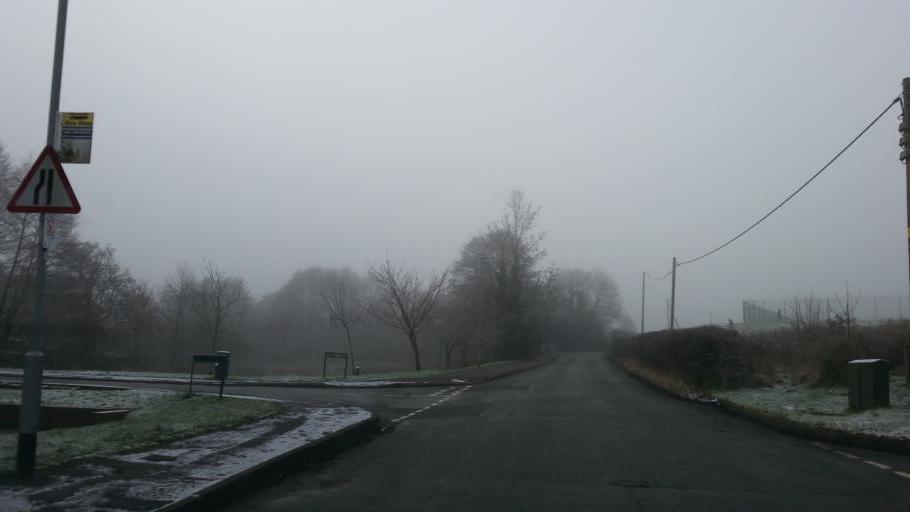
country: GB
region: England
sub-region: Staffordshire
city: Biddulph
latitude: 53.1227
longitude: -2.1721
